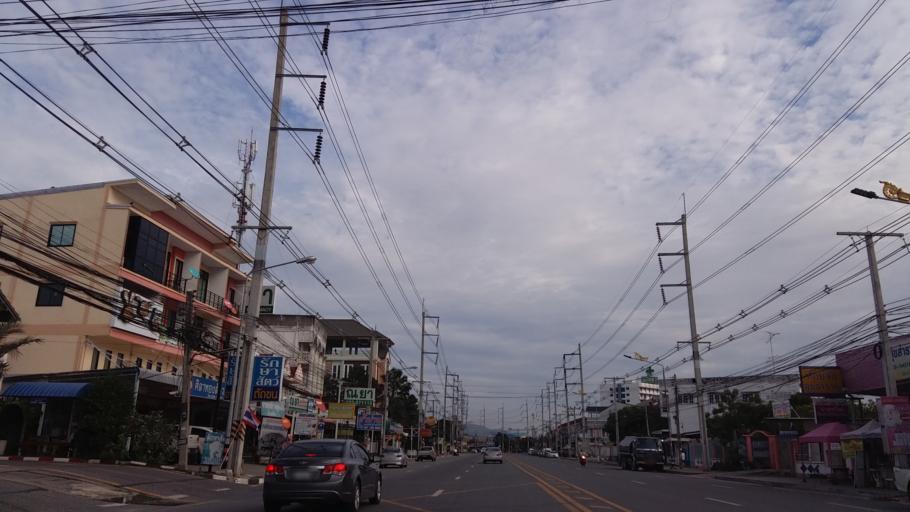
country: TH
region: Chon Buri
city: Chon Buri
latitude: 13.3211
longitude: 100.9463
